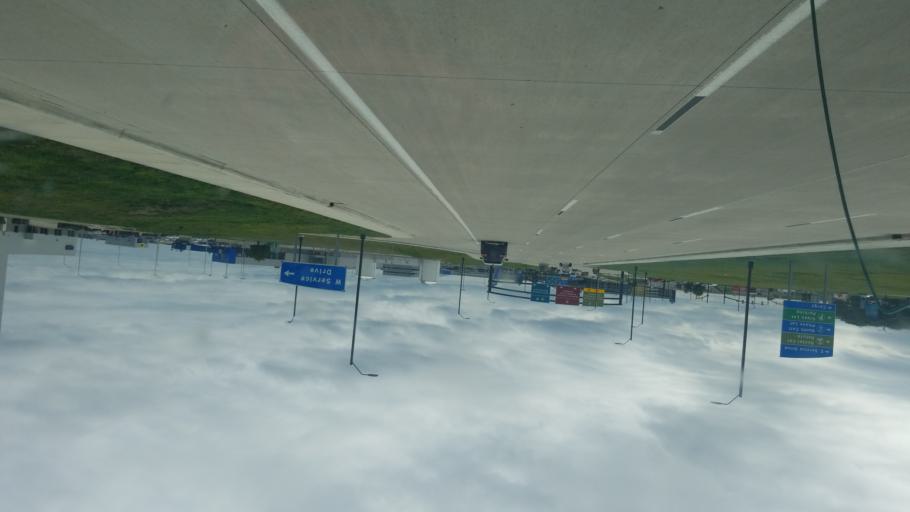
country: US
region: Michigan
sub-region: Wayne County
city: Romulus
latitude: 42.2324
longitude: -83.3419
